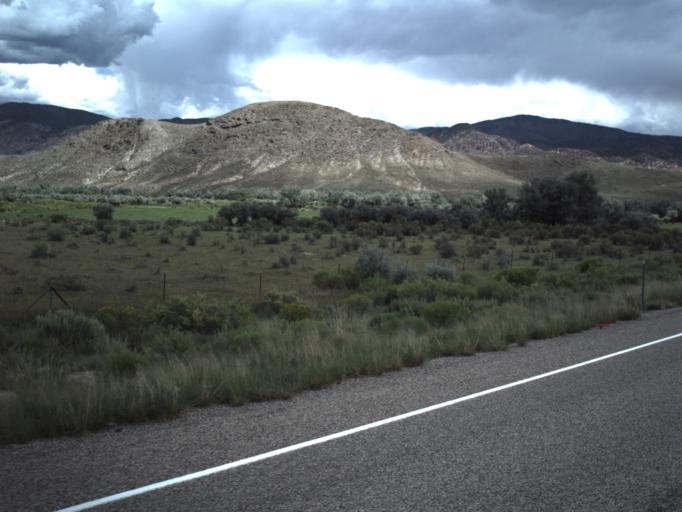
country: US
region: Utah
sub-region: Piute County
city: Junction
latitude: 38.2084
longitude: -112.2117
